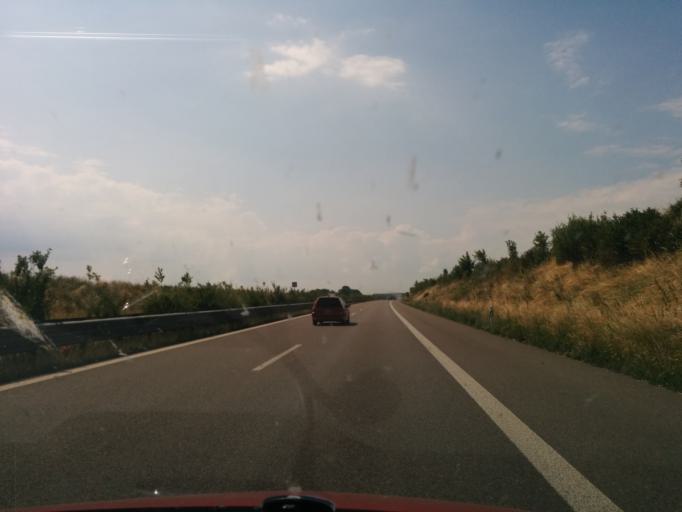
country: DE
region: Bavaria
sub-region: Upper Bavaria
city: Hurlach
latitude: 48.1334
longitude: 10.8323
